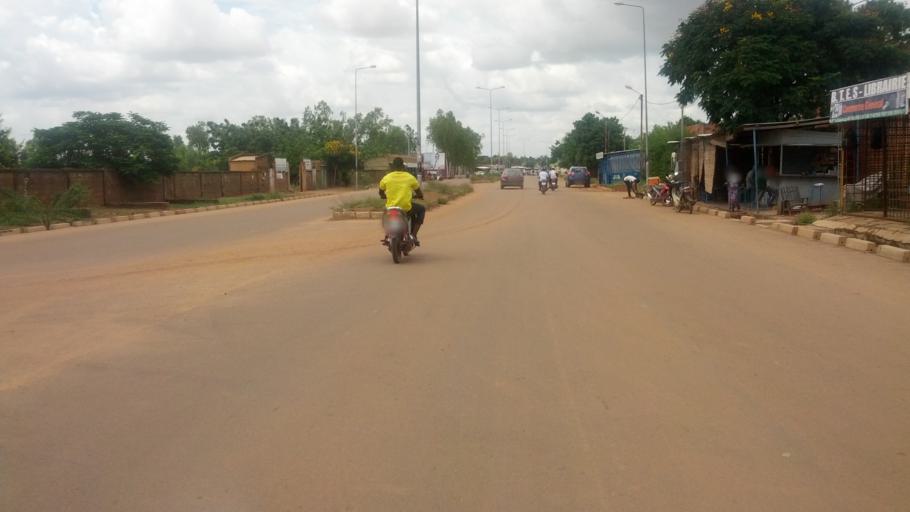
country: BF
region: Centre
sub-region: Kadiogo Province
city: Ouagadougou
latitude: 12.3704
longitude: -1.4976
